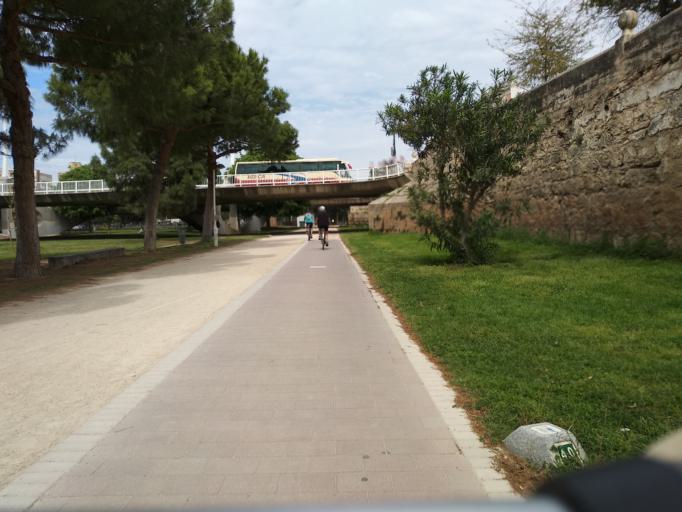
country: ES
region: Valencia
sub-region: Provincia de Valencia
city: Valencia
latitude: 39.4802
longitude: -0.3838
